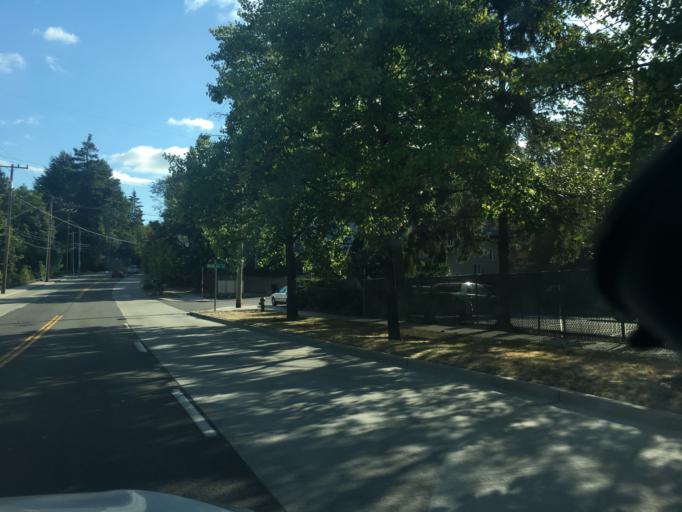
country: US
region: Washington
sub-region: King County
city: Shoreline
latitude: 47.7081
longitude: -122.3353
